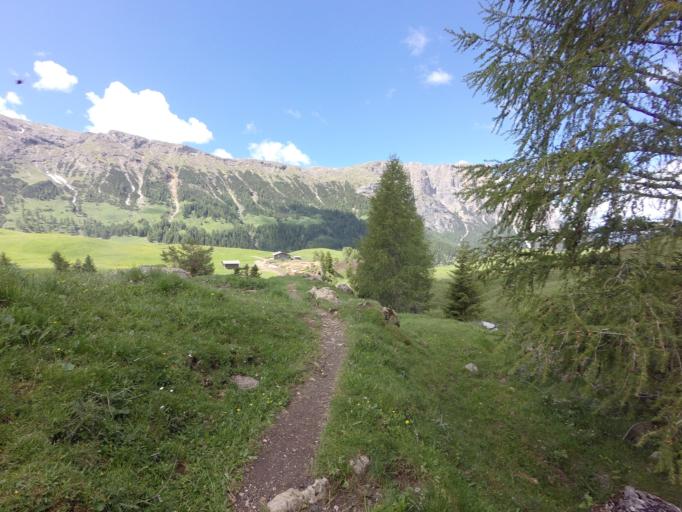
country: IT
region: Trentino-Alto Adige
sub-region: Bolzano
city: Siusi
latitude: 46.5194
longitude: 11.6123
